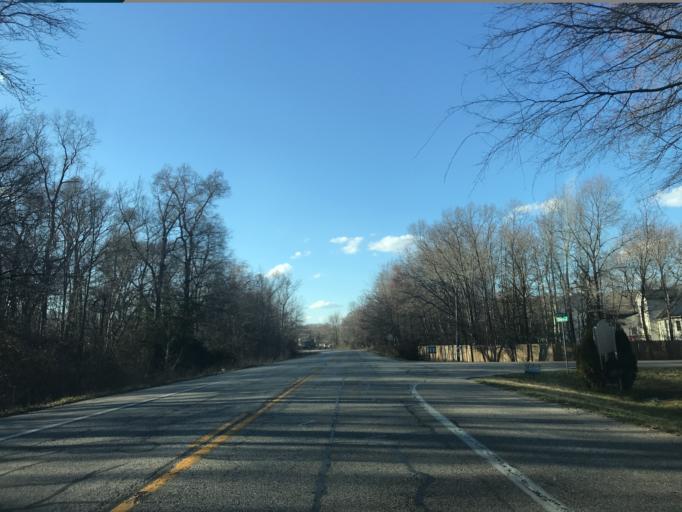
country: US
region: Maryland
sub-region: Anne Arundel County
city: Mayo
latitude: 38.8996
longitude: -76.5146
